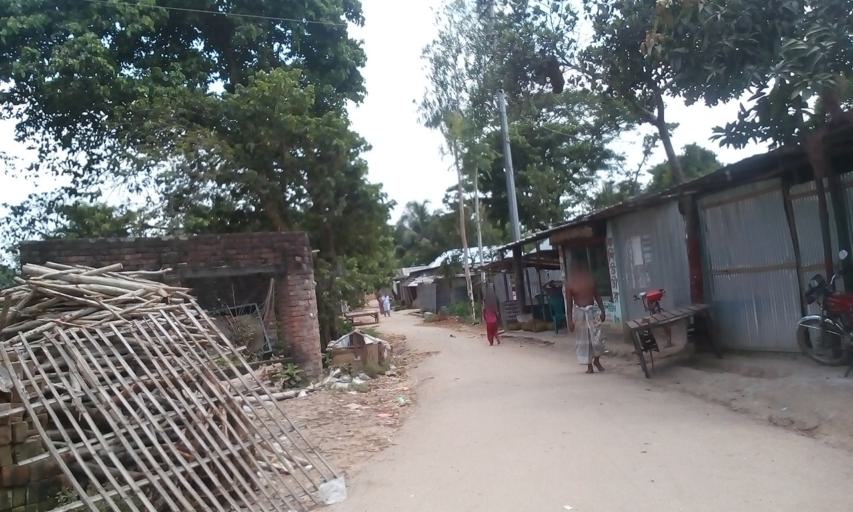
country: IN
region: West Bengal
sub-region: Dakshin Dinajpur
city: Balurghat
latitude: 25.3938
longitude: 88.9900
